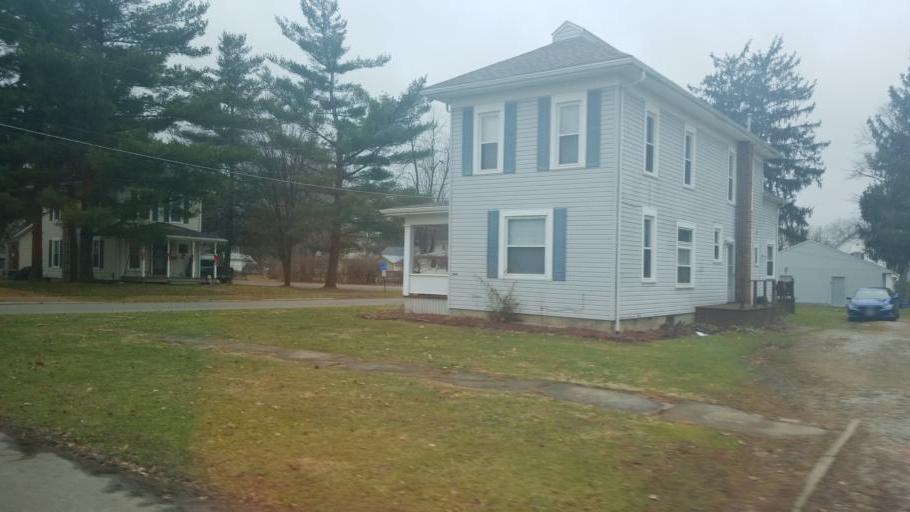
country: US
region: Ohio
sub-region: Crawford County
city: Galion
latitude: 40.7247
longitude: -82.7915
